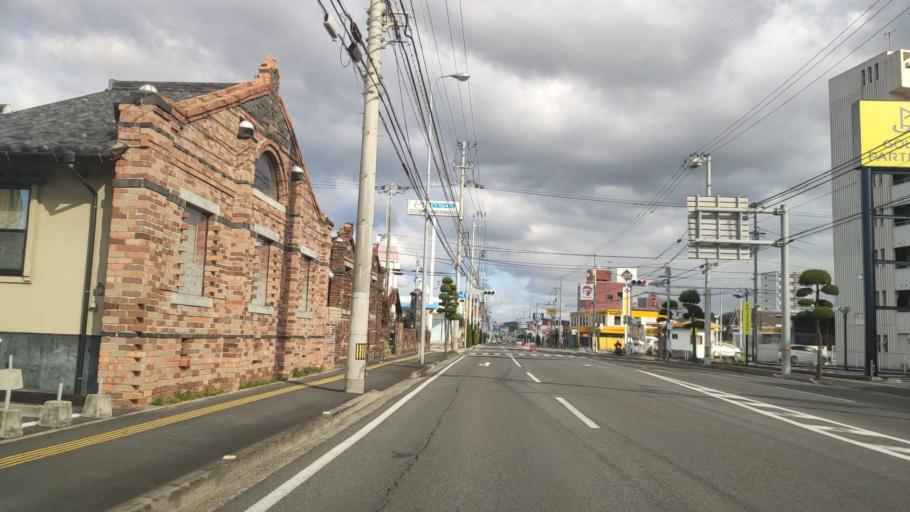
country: JP
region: Ehime
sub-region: Shikoku-chuo Shi
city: Matsuyama
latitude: 33.8575
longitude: 132.7485
